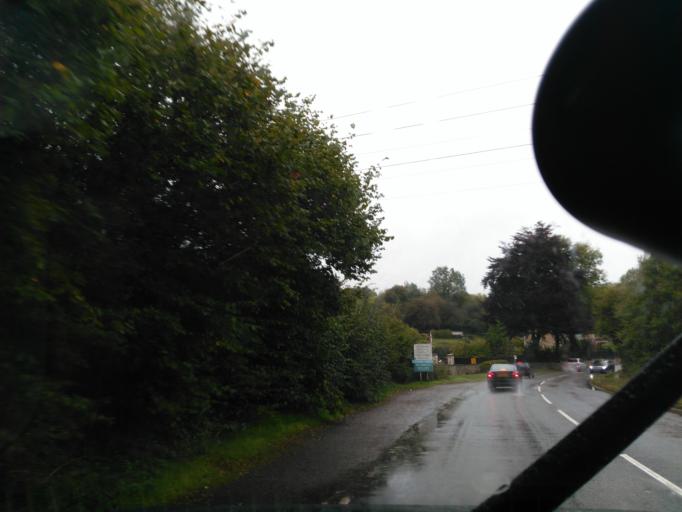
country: GB
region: England
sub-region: Wiltshire
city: Chippenham
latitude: 51.4423
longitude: -2.1348
